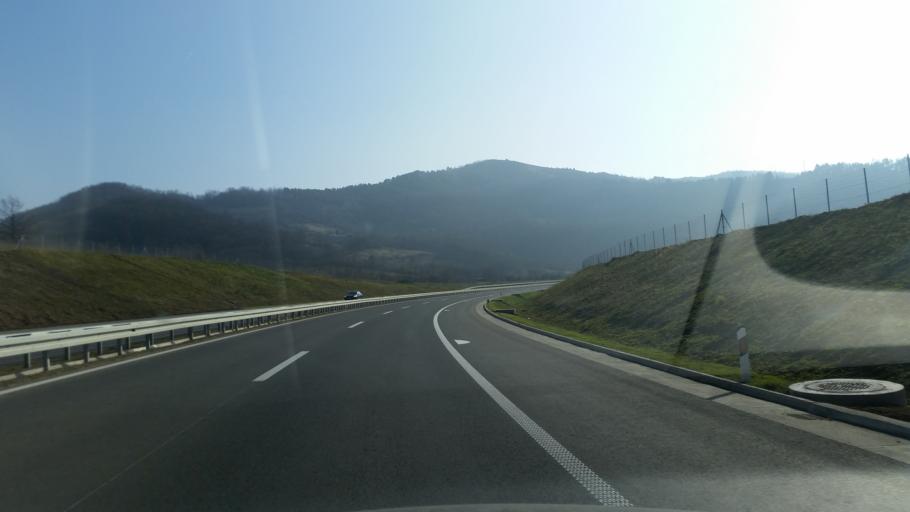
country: RS
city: Prislonica
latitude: 44.0004
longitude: 20.4014
